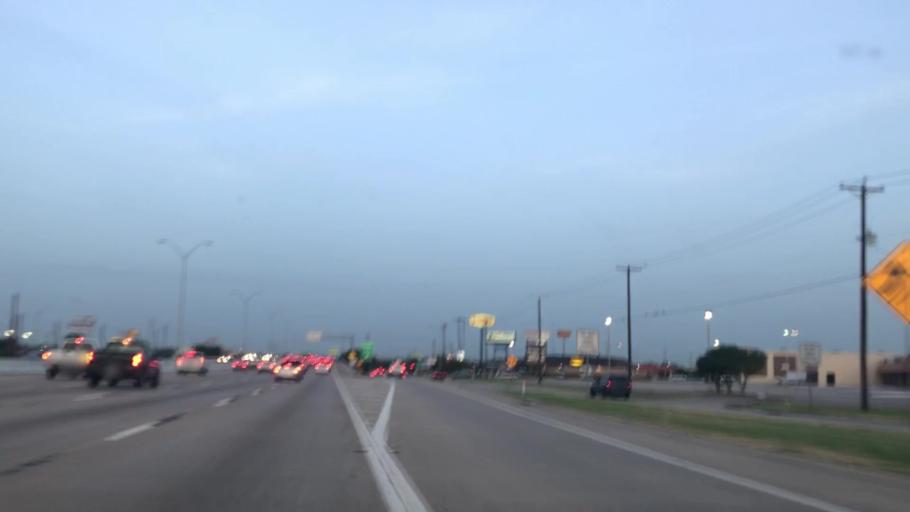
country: US
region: Texas
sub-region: Dallas County
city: Sunnyvale
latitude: 32.8419
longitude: -96.5913
